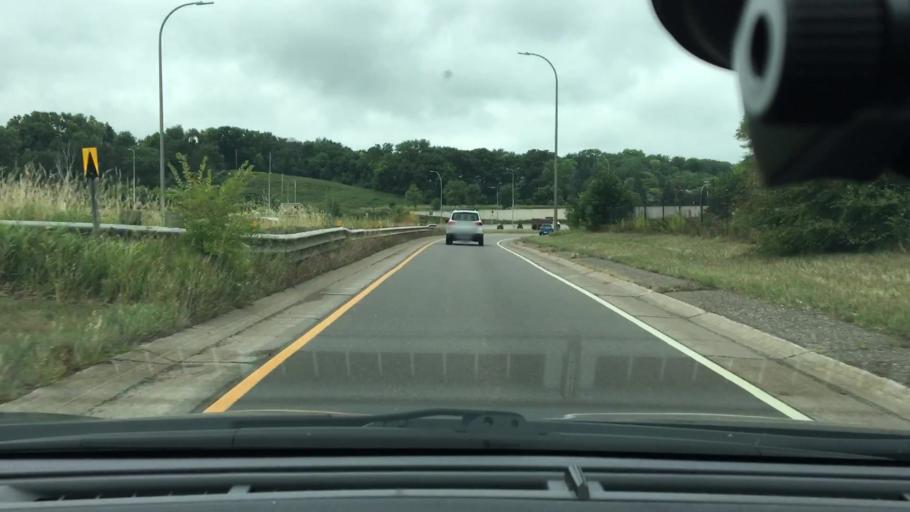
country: US
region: Minnesota
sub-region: Hennepin County
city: Minnetonka Mills
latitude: 44.9747
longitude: -93.4018
